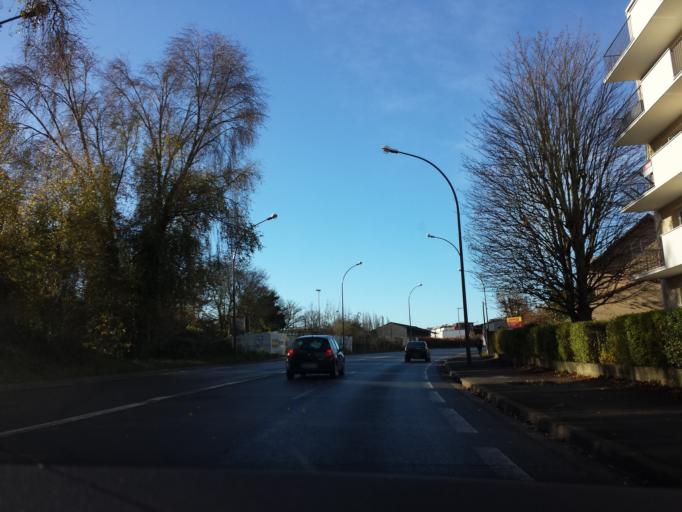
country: FR
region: Ile-de-France
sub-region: Departement de l'Essonne
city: Verrieres-le-Buisson
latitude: 48.7312
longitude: 2.2645
